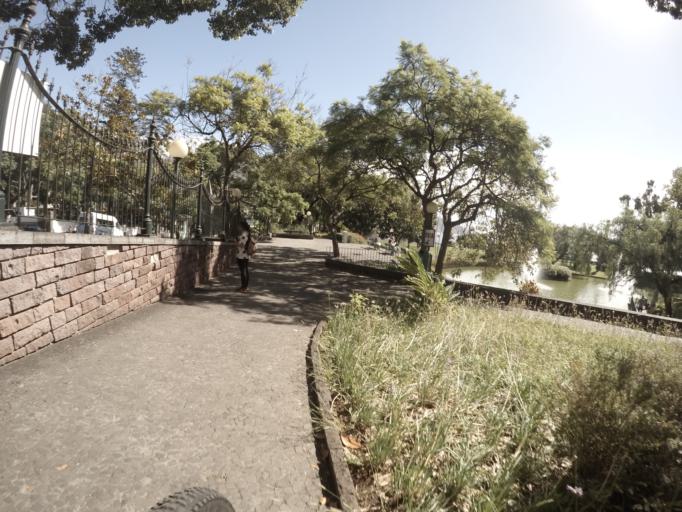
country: PT
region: Madeira
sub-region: Funchal
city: Funchal
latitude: 32.6456
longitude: -16.9150
